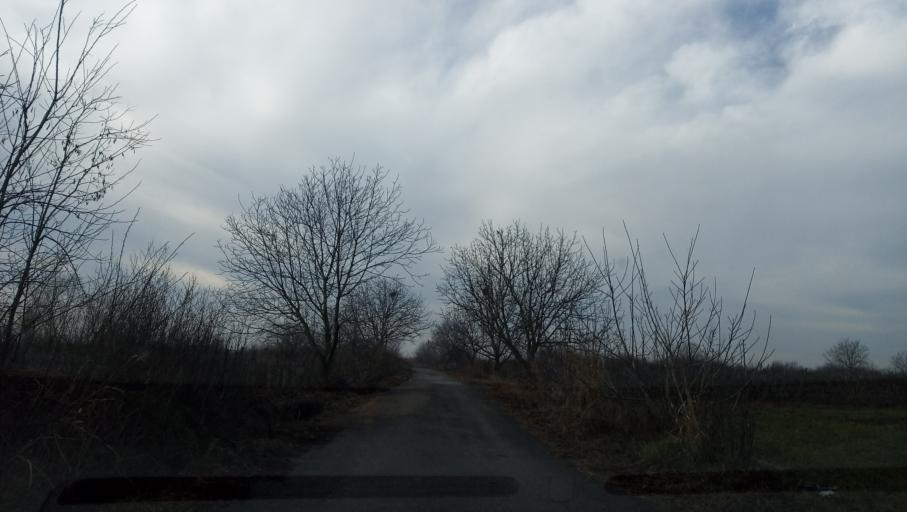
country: RO
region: Giurgiu
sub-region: Comuna Herasti
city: Herasti
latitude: 44.2205
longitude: 26.3604
